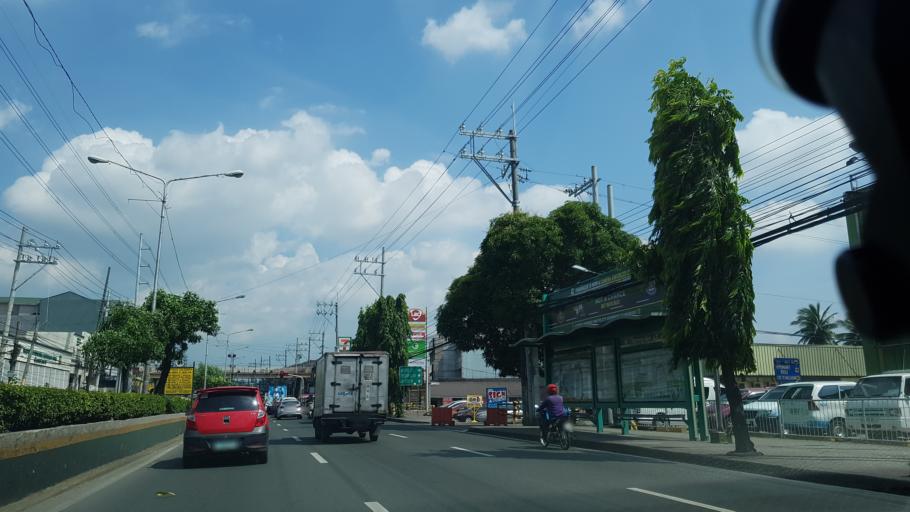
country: PH
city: Sambayanihan People's Village
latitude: 14.4692
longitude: 121.0107
